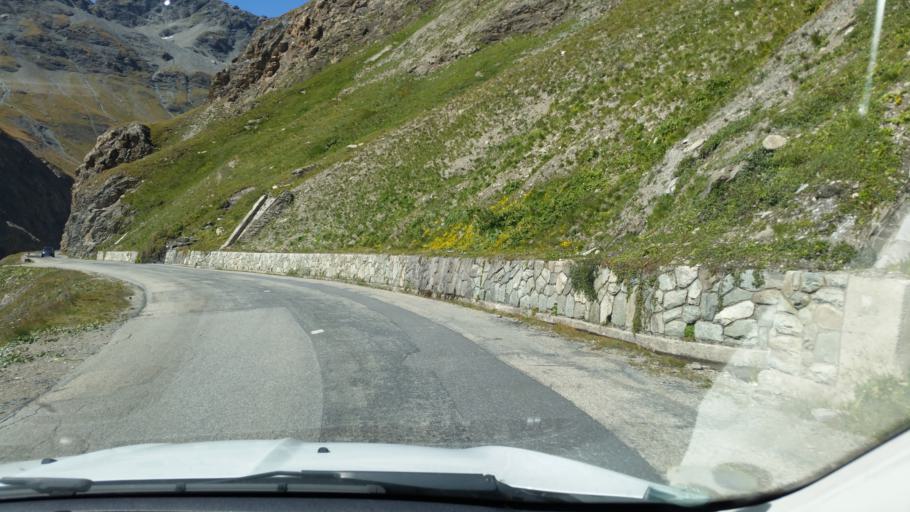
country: FR
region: Rhone-Alpes
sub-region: Departement de la Savoie
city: Val-d'Isere
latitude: 45.4023
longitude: 7.0356
